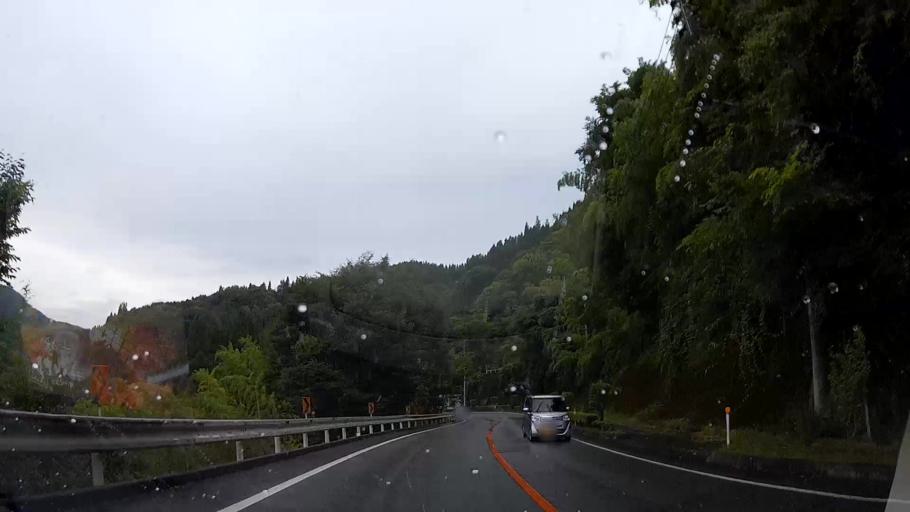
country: JP
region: Oita
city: Tsukawaki
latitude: 33.1547
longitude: 131.0530
